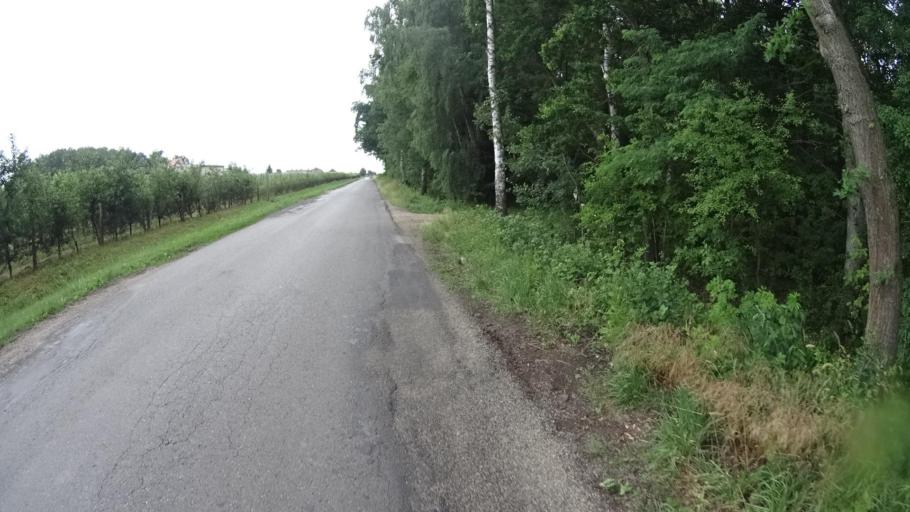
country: PL
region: Masovian Voivodeship
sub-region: Powiat grojecki
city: Goszczyn
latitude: 51.7771
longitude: 20.8535
